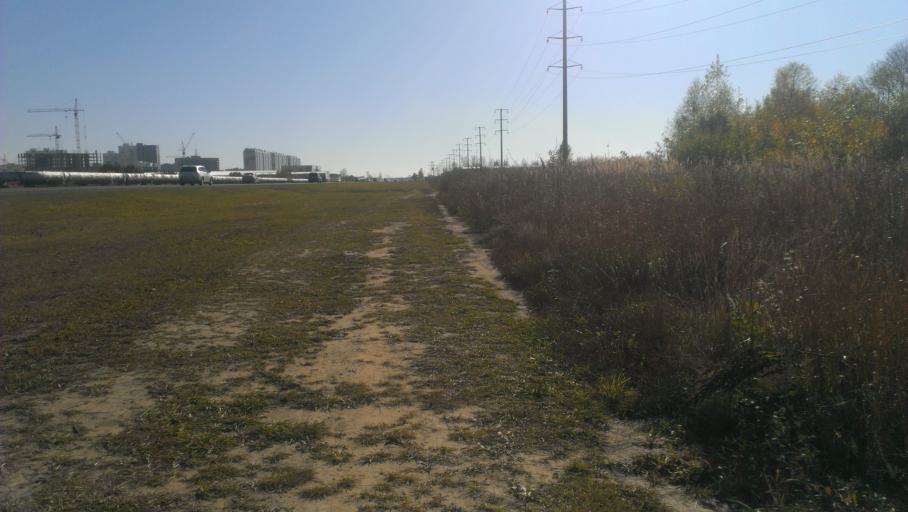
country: RU
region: Altai Krai
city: Novosilikatnyy
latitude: 53.3435
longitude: 83.6354
